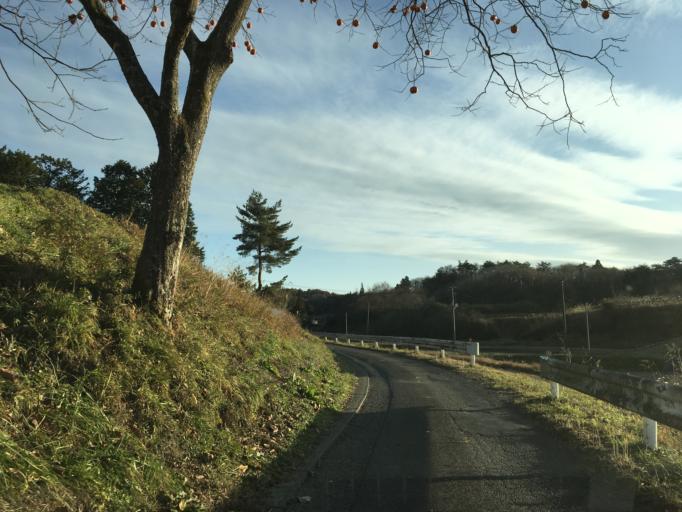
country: JP
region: Iwate
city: Ichinoseki
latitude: 38.9030
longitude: 141.1341
